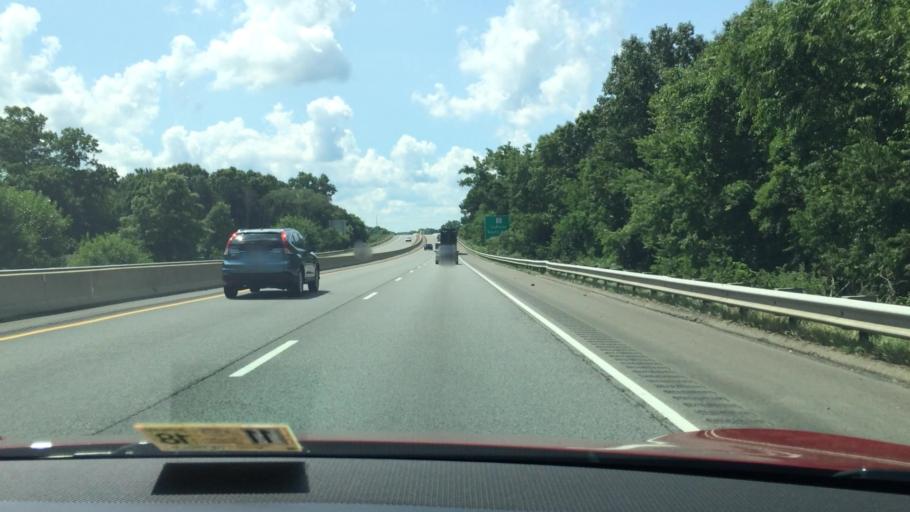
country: US
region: Indiana
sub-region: Saint Joseph County
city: South Bend
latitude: 41.6924
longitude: -86.3409
